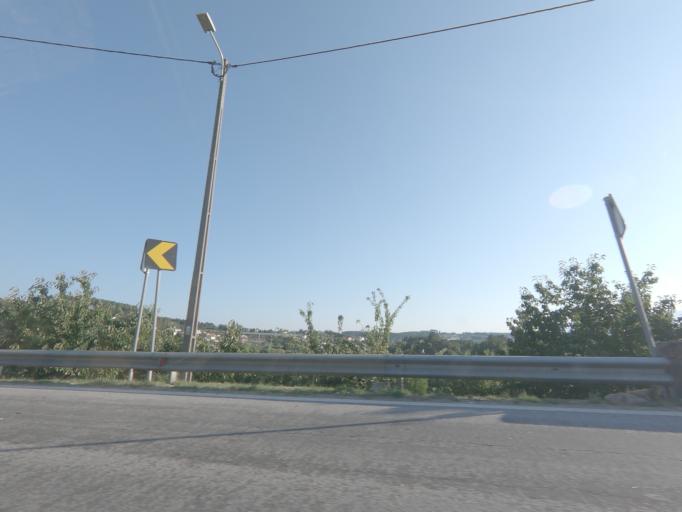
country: PT
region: Vila Real
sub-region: Vila Real
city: Vila Real
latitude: 41.2915
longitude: -7.7069
